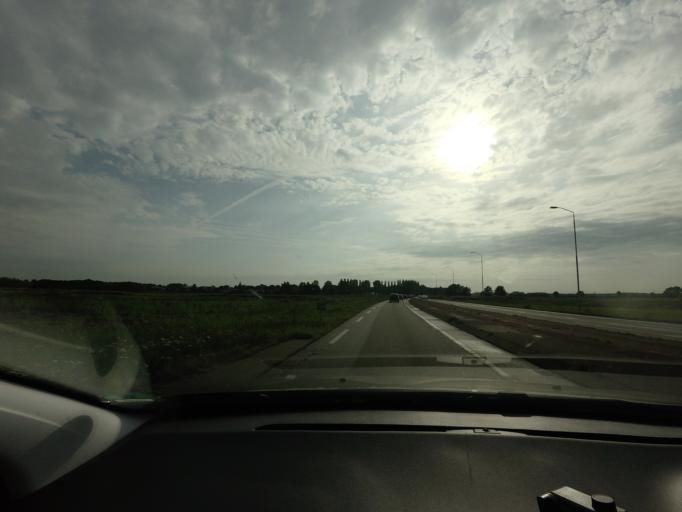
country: NL
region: North Brabant
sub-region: Gemeente Made en Drimmelen
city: Made
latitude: 51.6553
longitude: 4.7576
